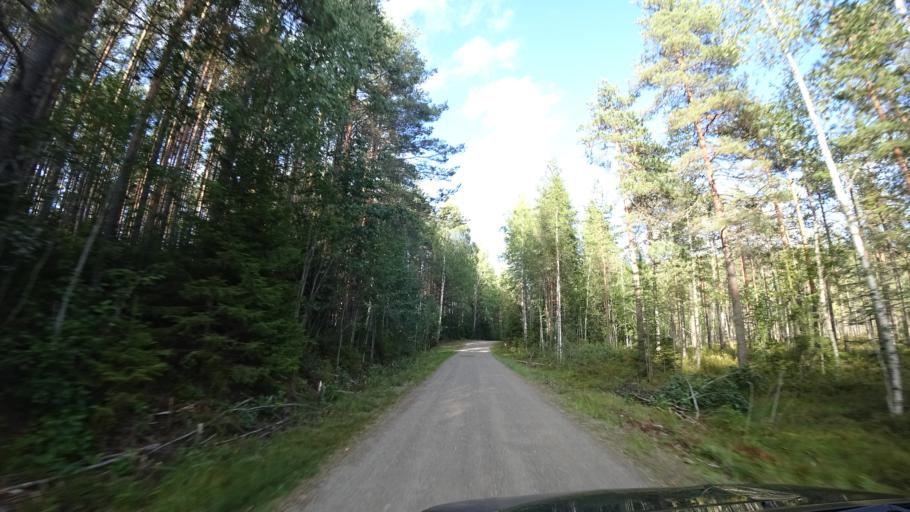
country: FI
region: Paijanne Tavastia
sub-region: Lahti
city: Auttoinen
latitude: 61.2225
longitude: 25.1871
